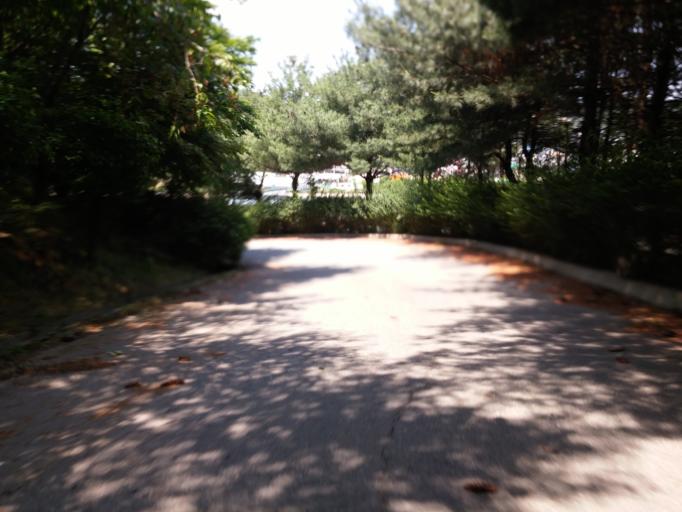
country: KR
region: Chungcheongbuk-do
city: Cheongju-si
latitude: 36.5580
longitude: 127.4365
